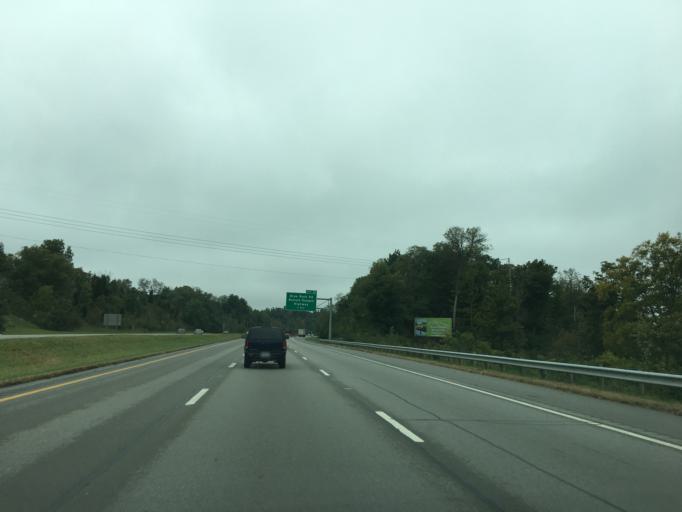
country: US
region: Ohio
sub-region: Hamilton County
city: Dry Ridge
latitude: 39.2486
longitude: -84.6110
